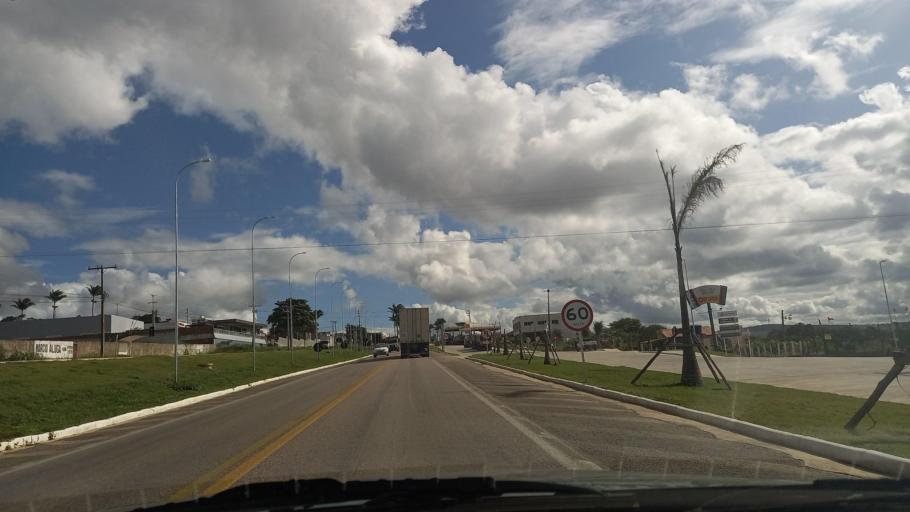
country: BR
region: Pernambuco
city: Garanhuns
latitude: -8.8722
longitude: -36.4670
